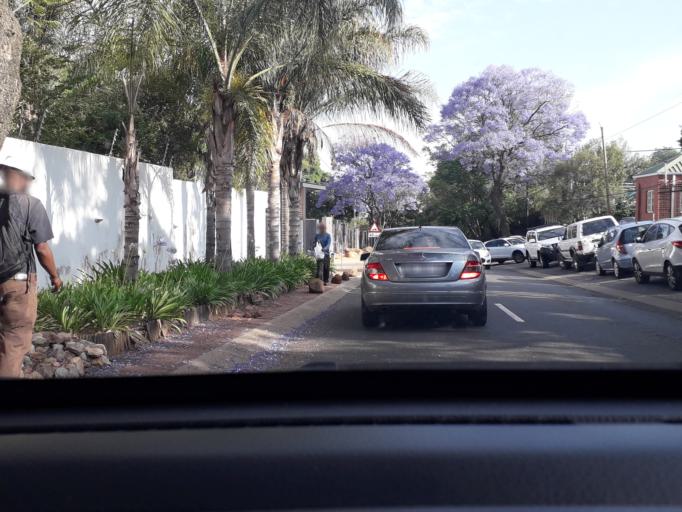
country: ZA
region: Gauteng
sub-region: City of Johannesburg Metropolitan Municipality
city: Modderfontein
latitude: -26.0794
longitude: 28.0582
